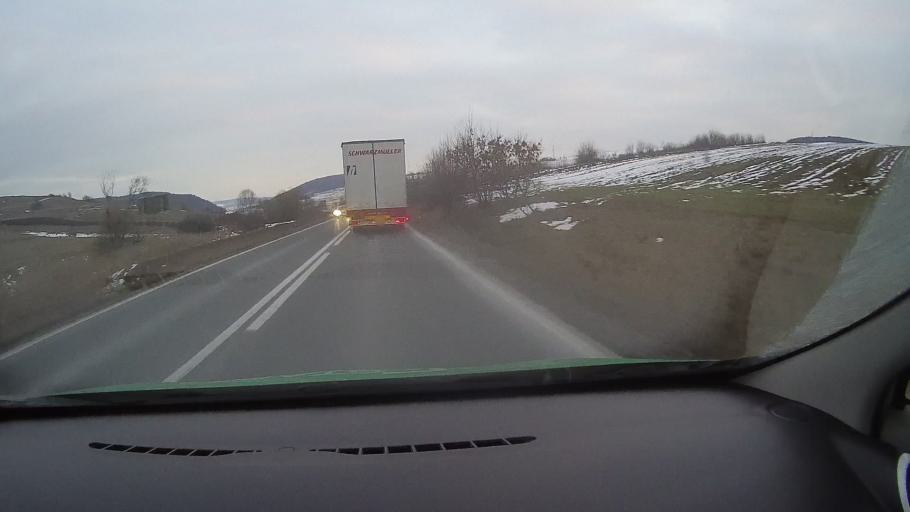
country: RO
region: Harghita
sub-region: Comuna Lupeni
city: Lupeni
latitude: 46.3495
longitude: 25.2635
